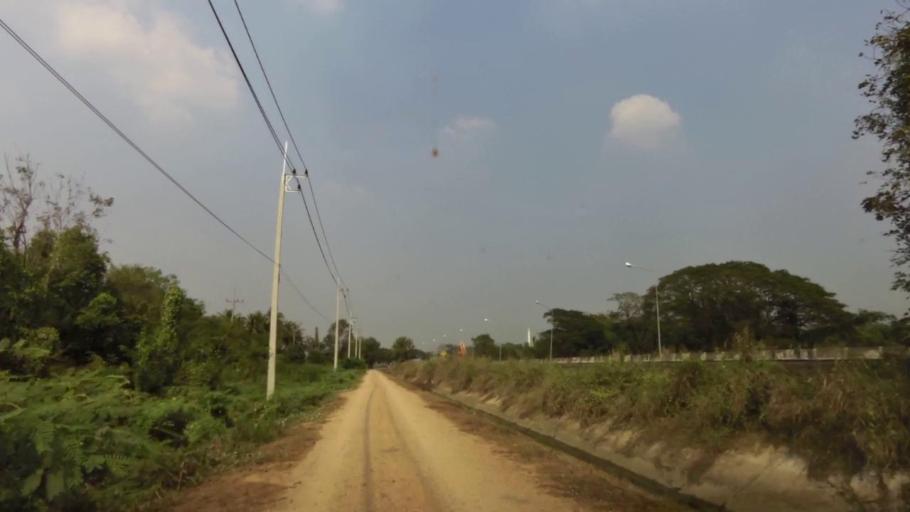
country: TH
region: Phra Nakhon Si Ayutthaya
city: Phra Nakhon Si Ayutthaya
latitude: 14.3085
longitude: 100.5628
